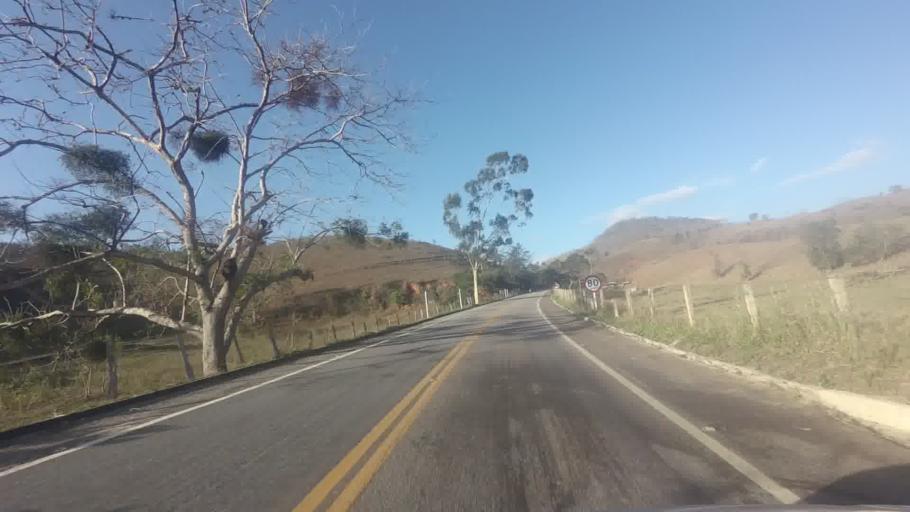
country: BR
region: Espirito Santo
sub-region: Jeronimo Monteiro
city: Jeronimo Monteiro
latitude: -20.8775
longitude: -41.2672
